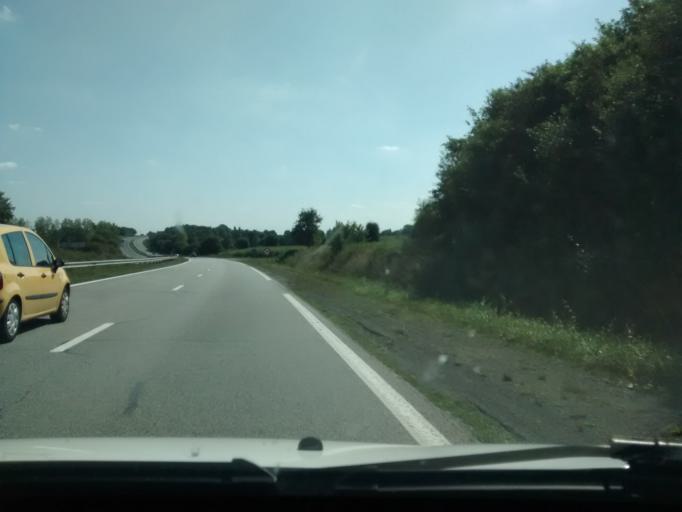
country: FR
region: Brittany
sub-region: Departement d'Ille-et-Vilaine
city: Quedillac
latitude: 48.2381
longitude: -2.1263
